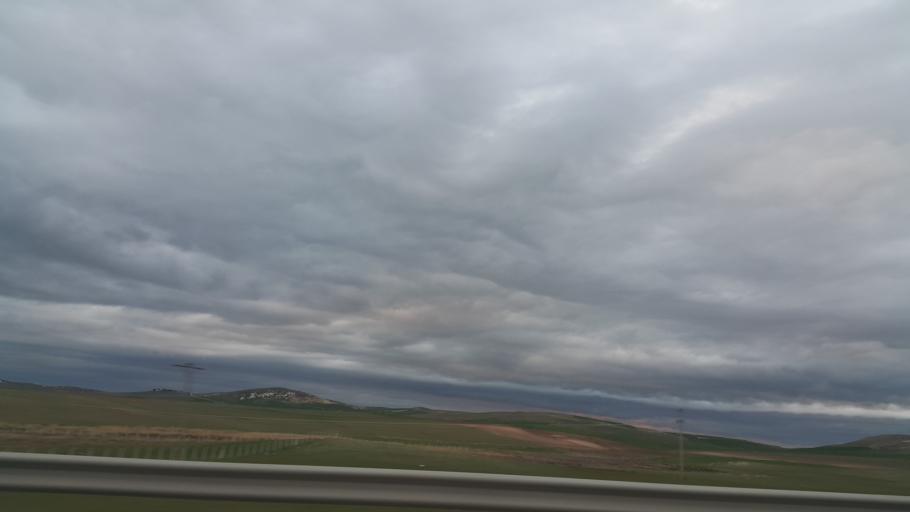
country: TR
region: Ankara
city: Ikizce
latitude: 39.5603
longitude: 32.8570
